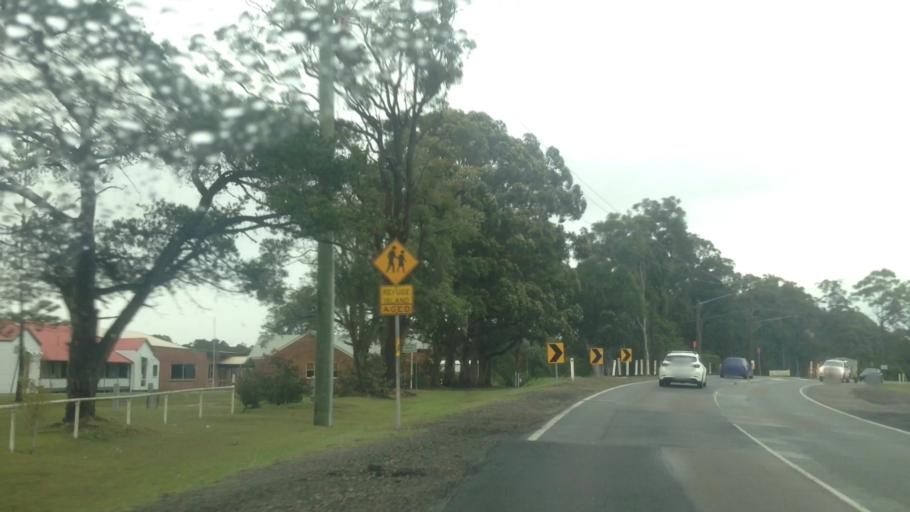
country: AU
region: New South Wales
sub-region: Wyong Shire
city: Charmhaven
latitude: -33.1690
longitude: 151.4762
